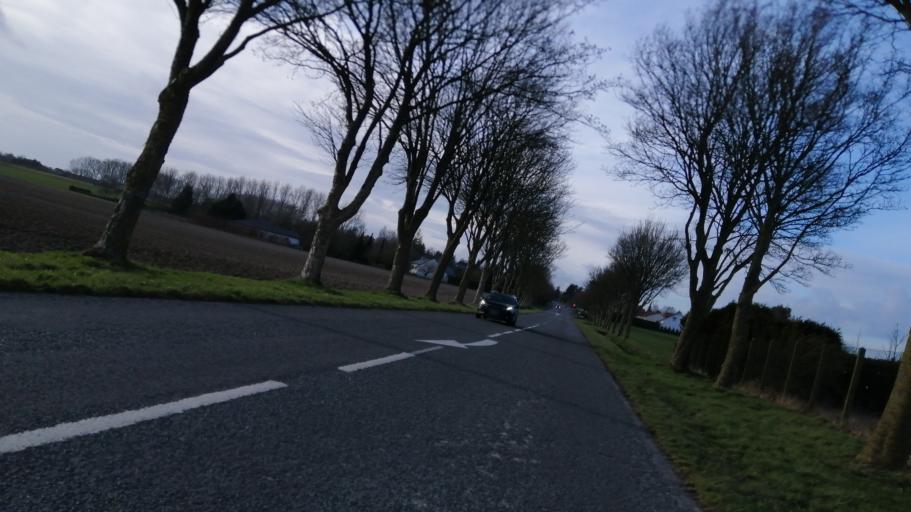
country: FR
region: Nord-Pas-de-Calais
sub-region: Departement du Pas-de-Calais
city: Beaurains
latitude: 50.2544
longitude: 2.8060
